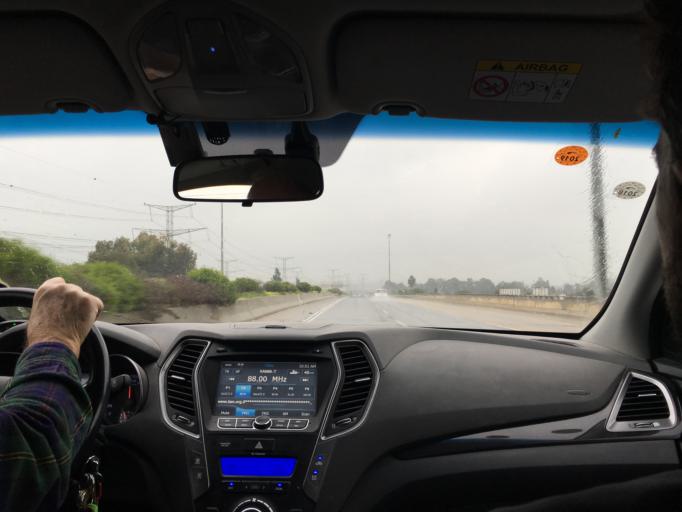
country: IL
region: Central District
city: Petah Tiqwa
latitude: 32.1215
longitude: 34.9025
